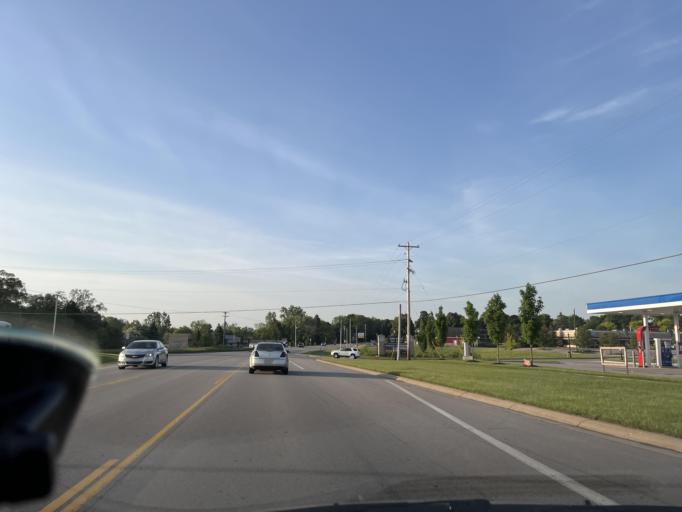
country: US
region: Michigan
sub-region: Barry County
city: Middleville
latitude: 42.7188
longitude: -85.4713
